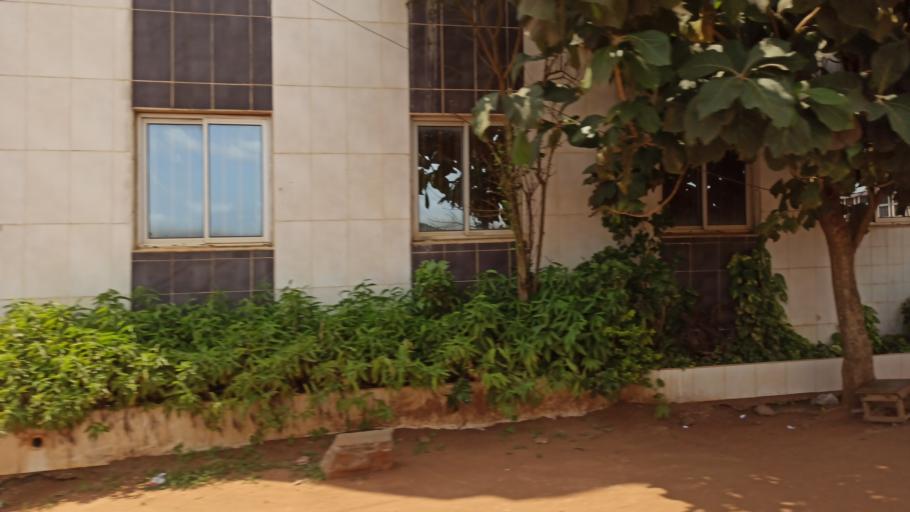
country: BJ
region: Queme
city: Porto-Novo
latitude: 6.4819
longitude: 2.6133
